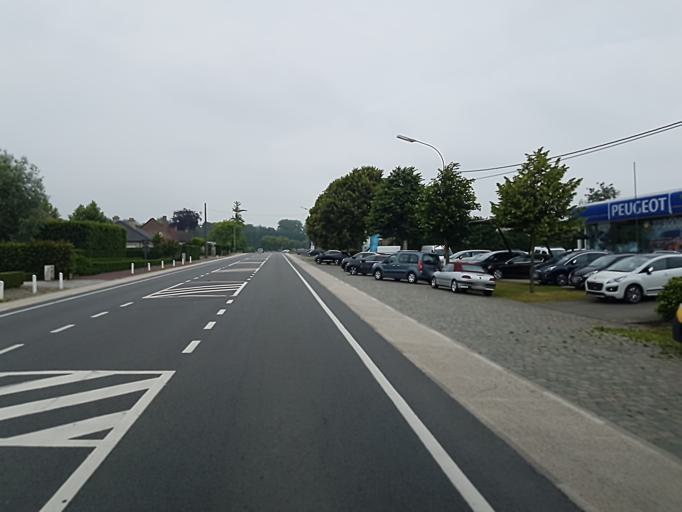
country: BE
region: Flanders
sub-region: Provincie West-Vlaanderen
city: Tielt
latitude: 50.9833
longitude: 3.3133
